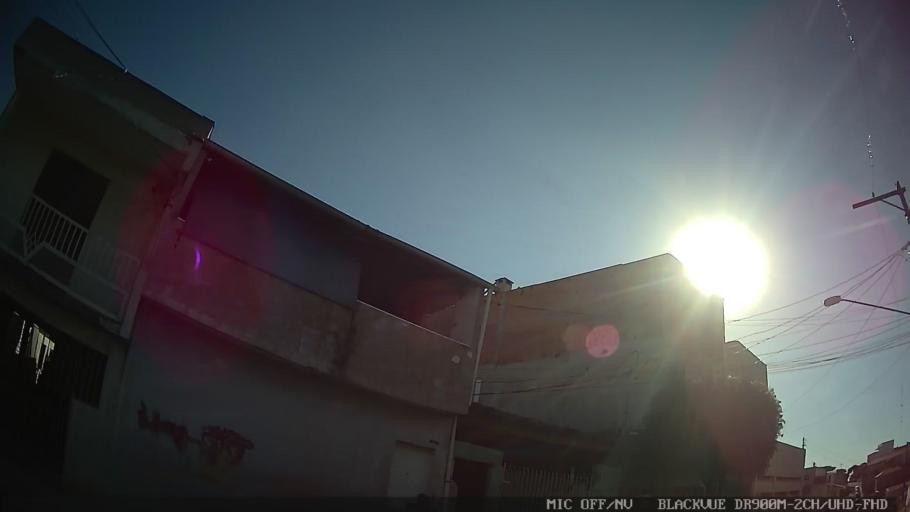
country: BR
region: Sao Paulo
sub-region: Sao Caetano Do Sul
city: Sao Caetano do Sul
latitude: -23.5486
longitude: -46.5218
